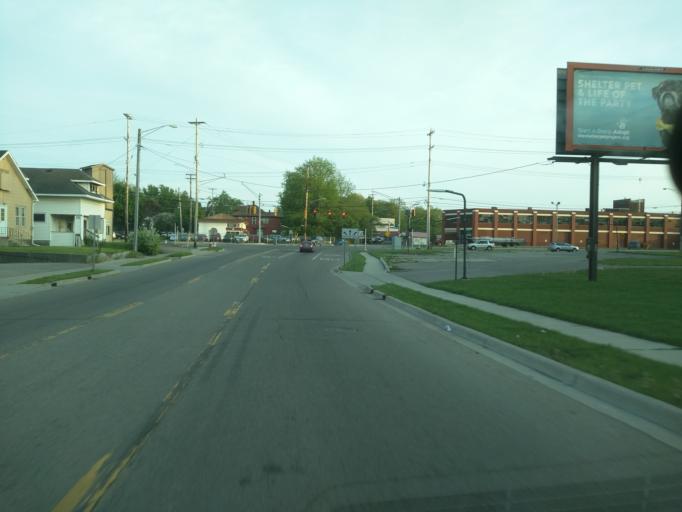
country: US
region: Michigan
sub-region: Ingham County
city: Lansing
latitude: 42.7127
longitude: -84.5525
